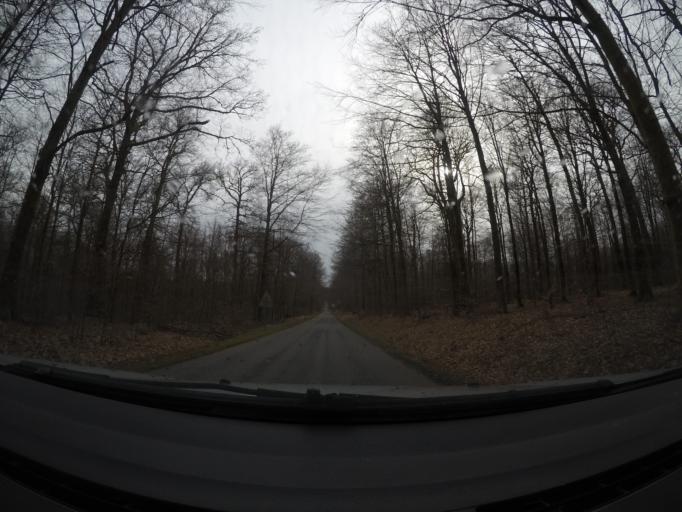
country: BE
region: Wallonia
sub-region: Province du Luxembourg
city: Fauvillers
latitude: 49.7816
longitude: 5.6837
